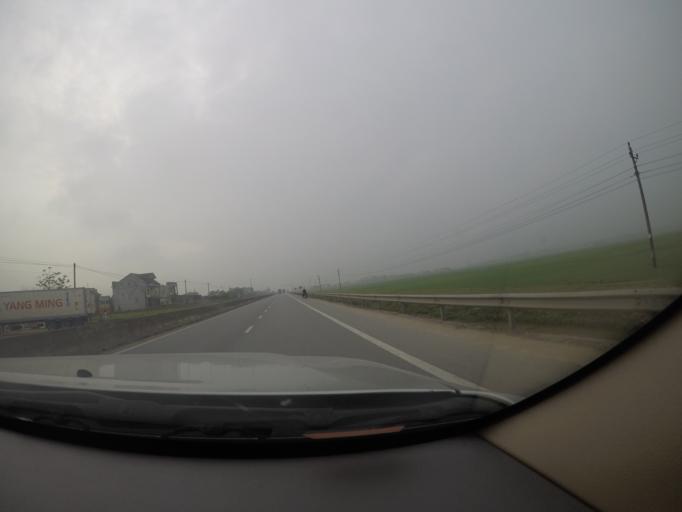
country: VN
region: Ha Tinh
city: Ky Anh
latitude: 18.1864
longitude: 106.1925
